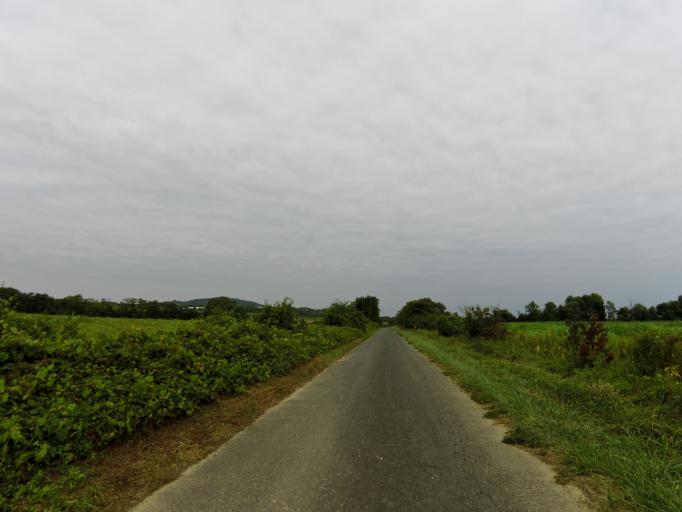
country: HU
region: Veszprem
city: Tapolca
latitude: 46.8429
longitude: 17.3652
